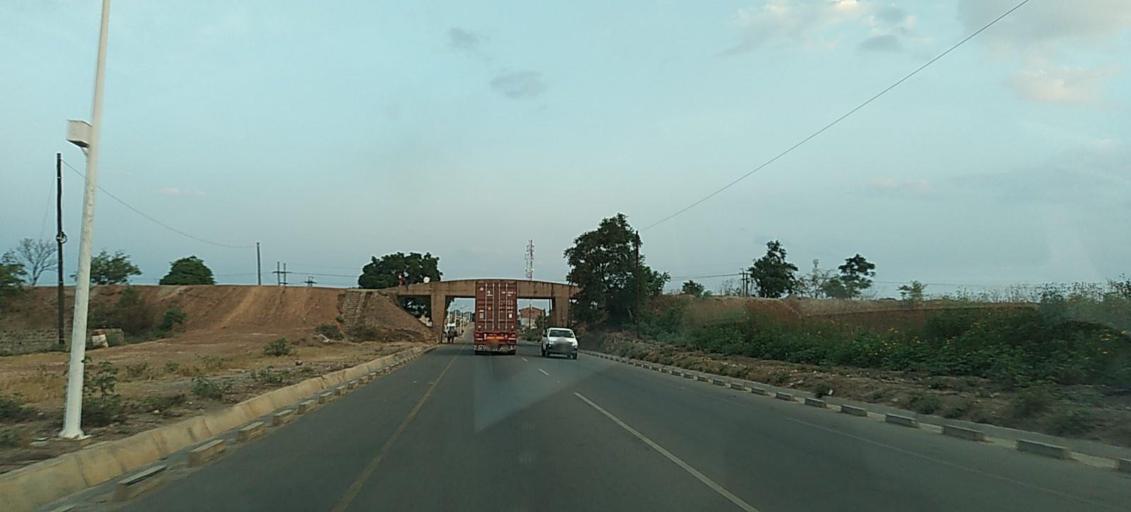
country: ZM
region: Copperbelt
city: Chingola
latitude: -12.5399
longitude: 27.8415
